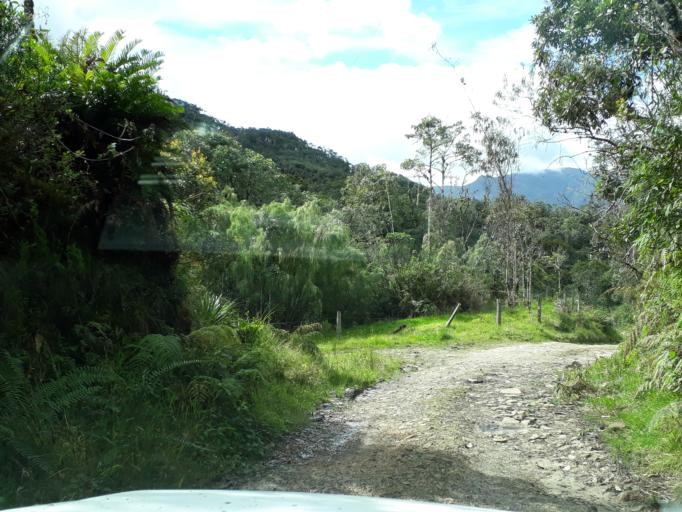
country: CO
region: Cundinamarca
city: Junin
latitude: 4.7838
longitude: -73.7750
